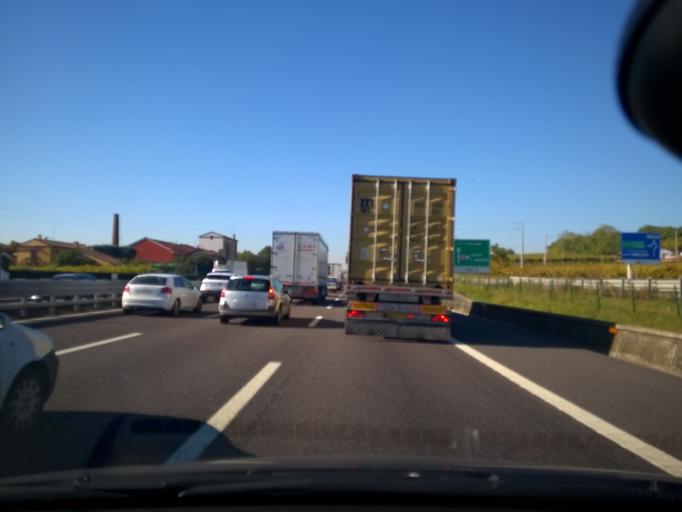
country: IT
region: Veneto
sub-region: Provincia di Verona
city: Soave
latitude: 45.4089
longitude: 11.2628
